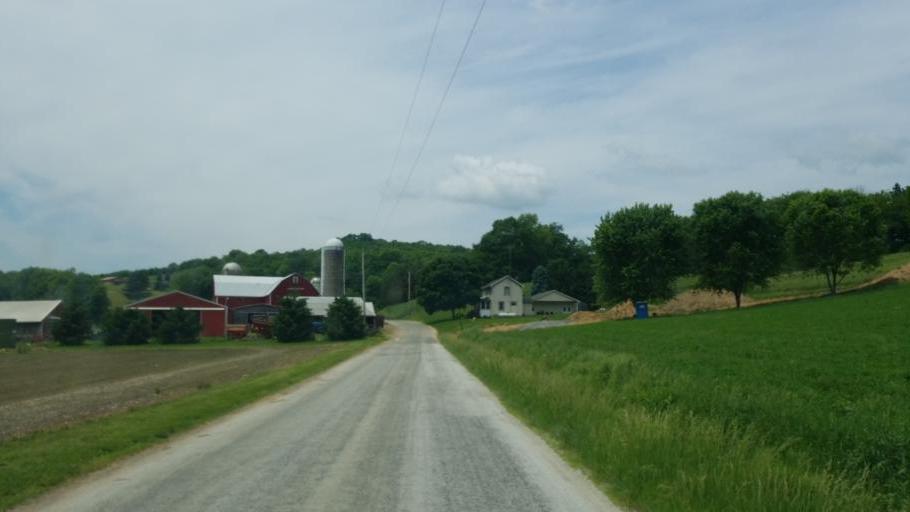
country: US
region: Ohio
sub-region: Coshocton County
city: West Lafayette
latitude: 40.3788
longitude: -81.7647
